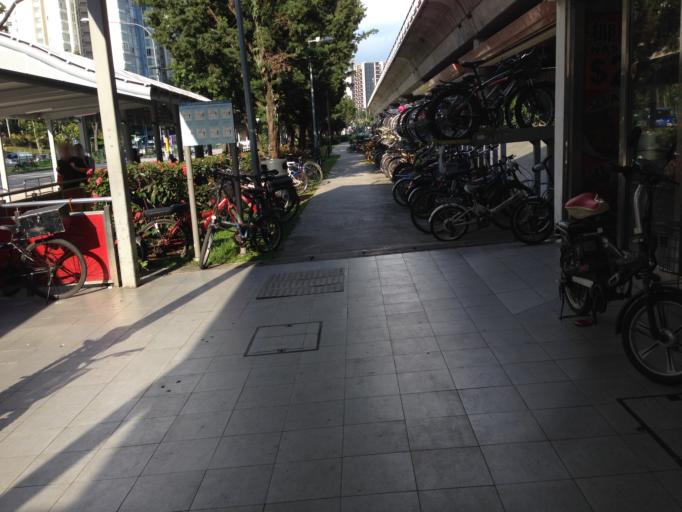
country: MY
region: Johor
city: Johor Bahru
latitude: 1.3446
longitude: 103.7205
